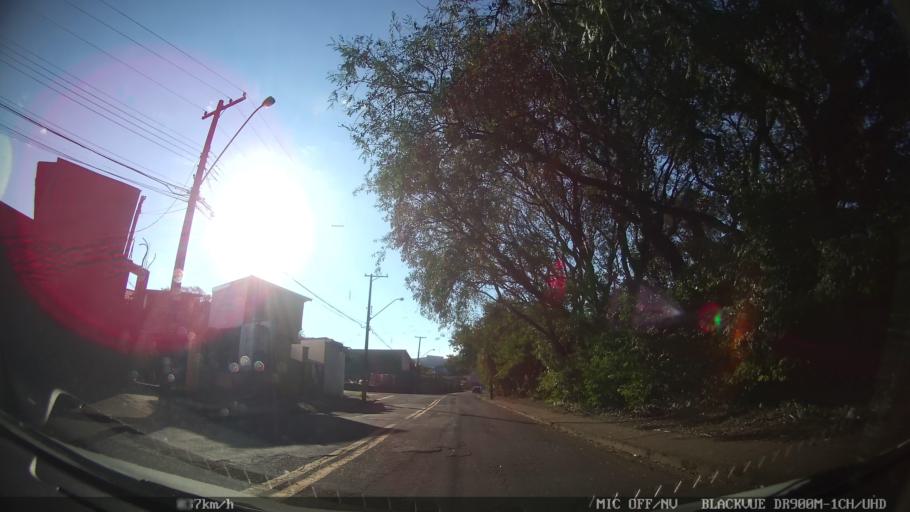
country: BR
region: Sao Paulo
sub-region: Piracicaba
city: Piracicaba
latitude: -22.6818
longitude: -47.6338
